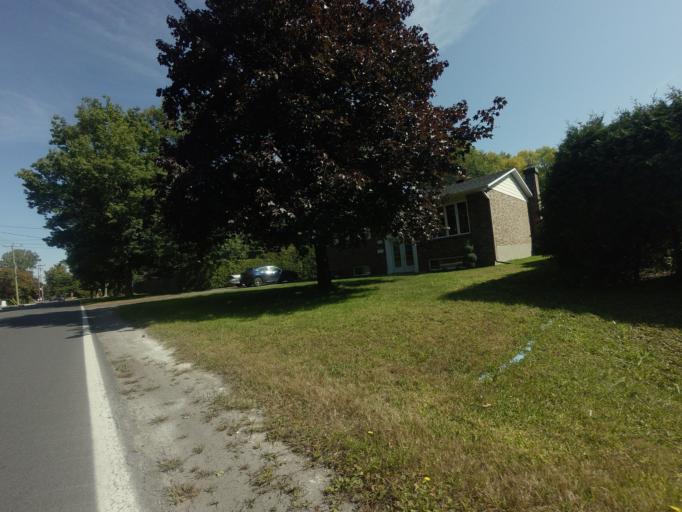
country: CA
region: Quebec
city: Dollard-Des Ormeaux
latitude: 45.4936
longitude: -73.8667
